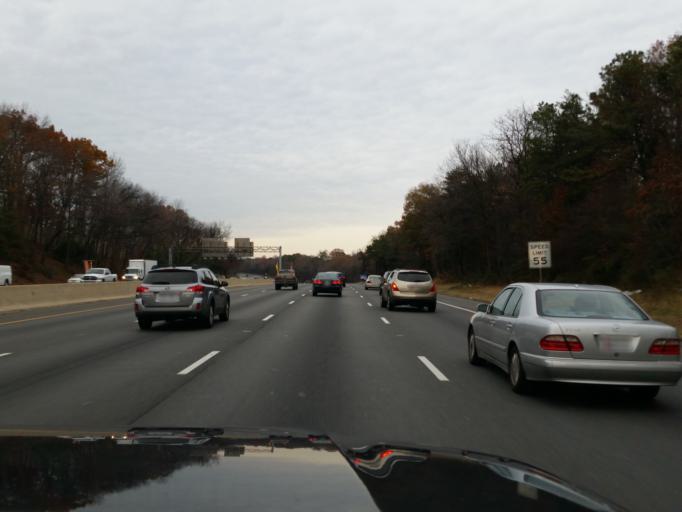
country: US
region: Maryland
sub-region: Prince George's County
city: Lanham
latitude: 38.9688
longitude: -76.8683
